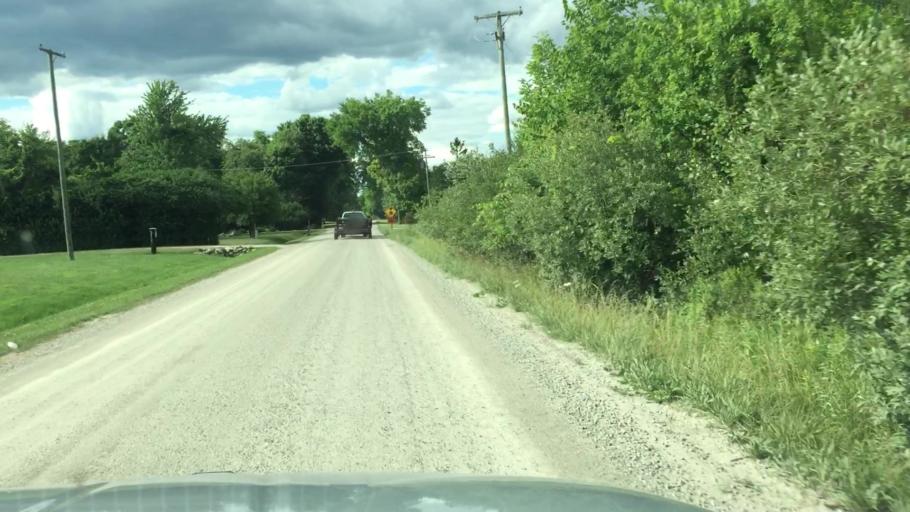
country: US
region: Michigan
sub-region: Saint Clair County
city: Yale
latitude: 43.1413
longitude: -82.8189
